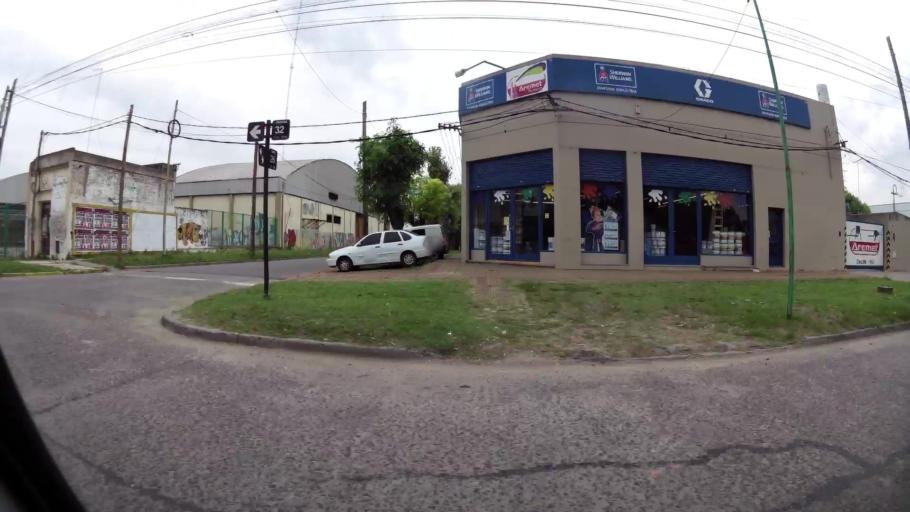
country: AR
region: Buenos Aires
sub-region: Partido de La Plata
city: La Plata
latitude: -34.9179
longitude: -57.9889
